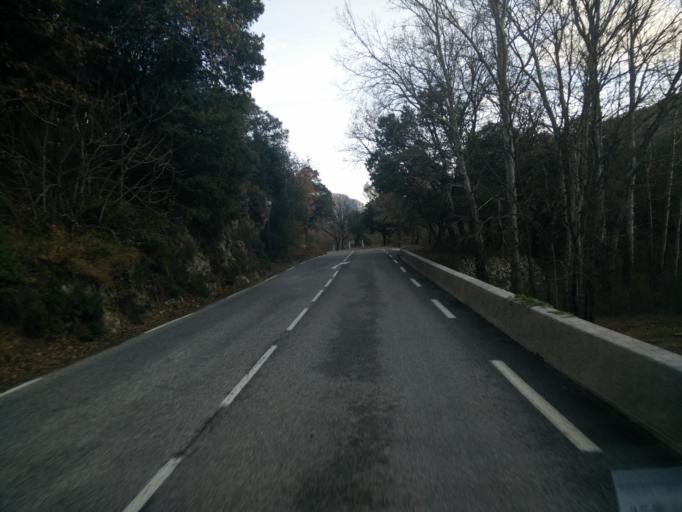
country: FR
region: Provence-Alpes-Cote d'Azur
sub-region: Departement du Var
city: Signes
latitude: 43.2825
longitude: 5.8991
